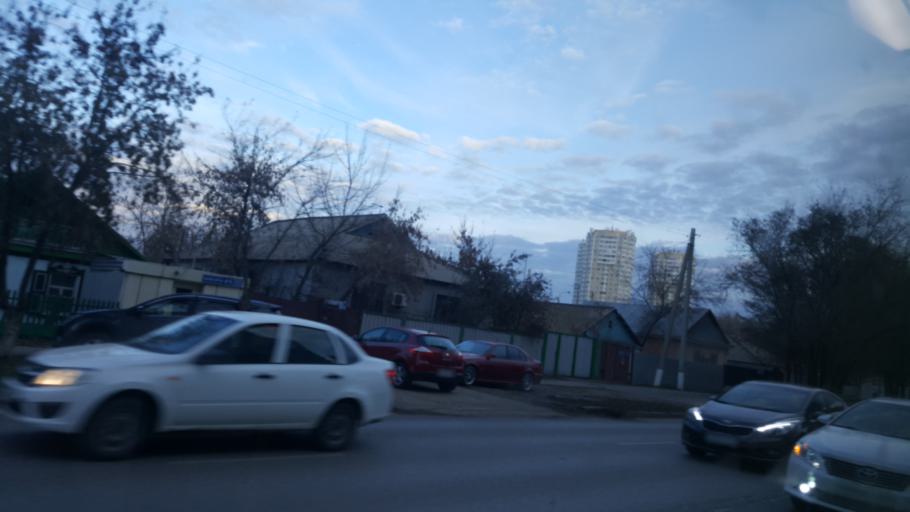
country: KZ
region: Astana Qalasy
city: Astana
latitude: 51.1637
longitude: 71.4600
